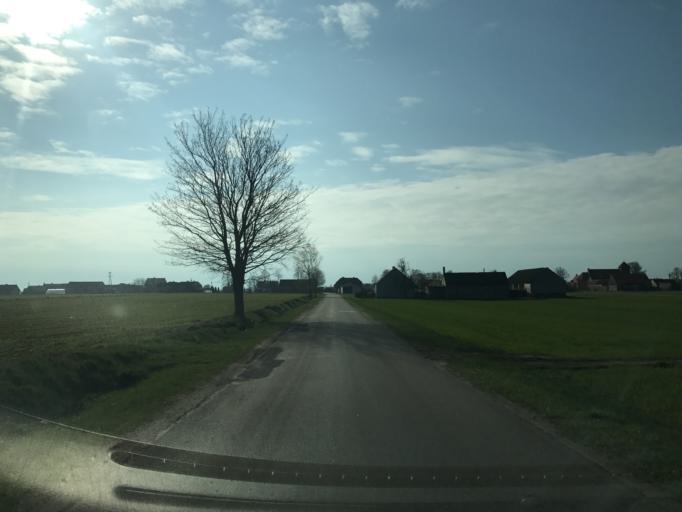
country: PL
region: Warmian-Masurian Voivodeship
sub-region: Powiat dzialdowski
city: Lidzbark
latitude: 53.3111
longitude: 19.8589
